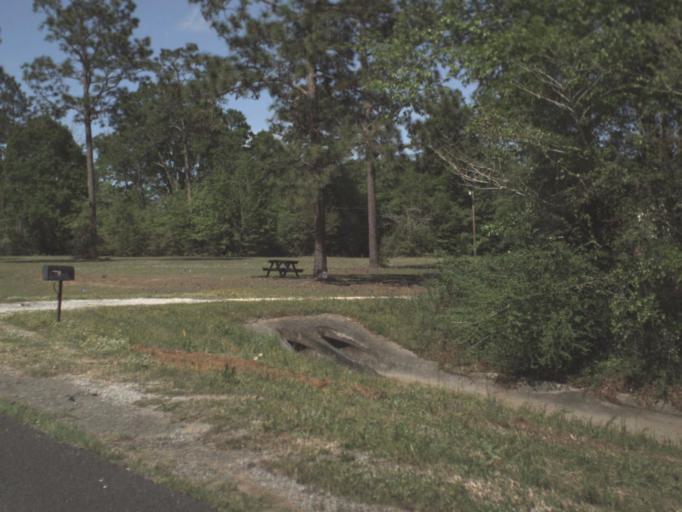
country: US
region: Florida
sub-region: Escambia County
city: Cantonment
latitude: 30.6584
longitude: -87.3515
